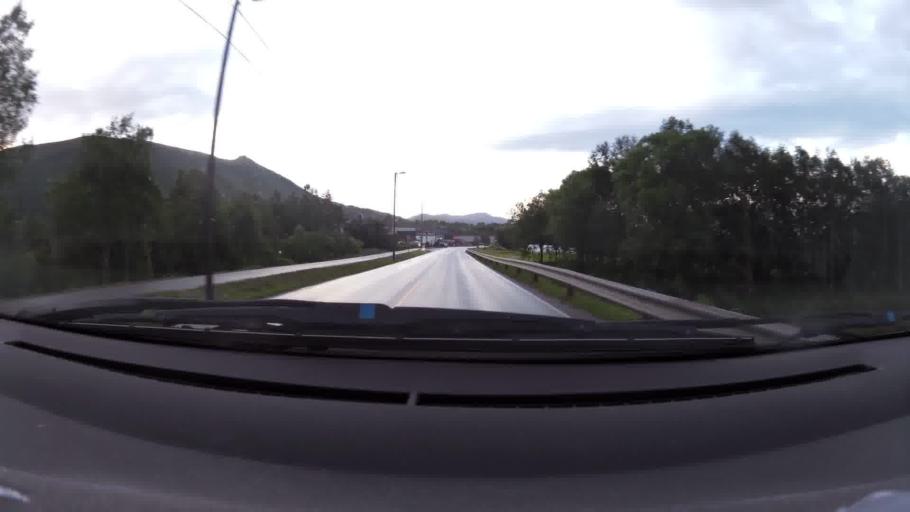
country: NO
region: More og Romsdal
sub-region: Eide
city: Eide
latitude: 62.9063
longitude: 7.4256
